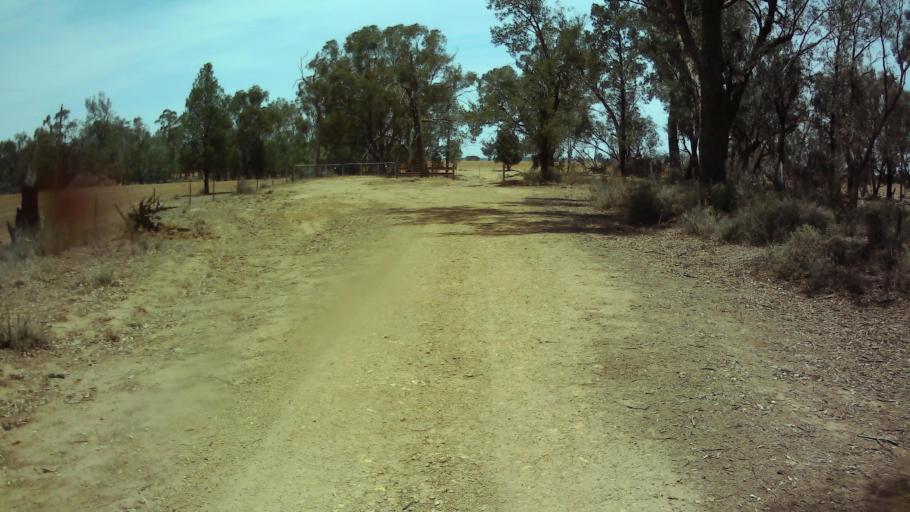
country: AU
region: New South Wales
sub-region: Weddin
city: Grenfell
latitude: -33.8450
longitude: 147.7250
